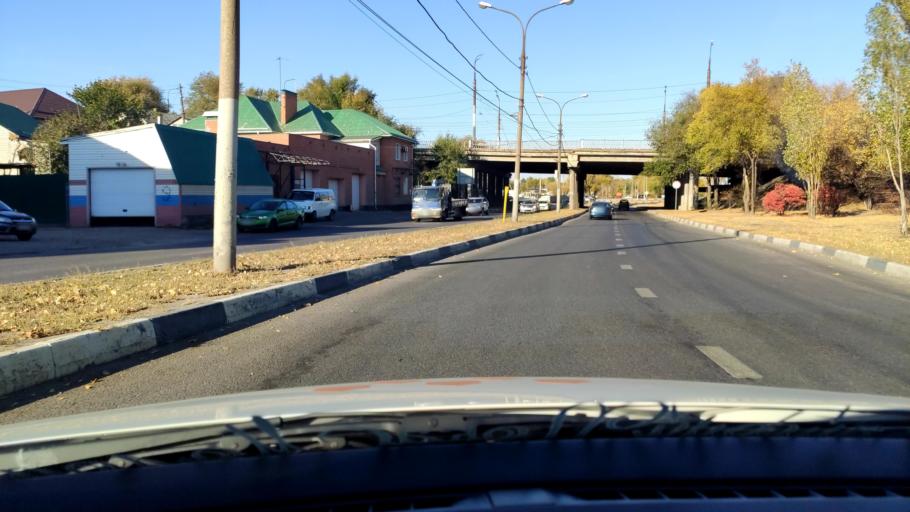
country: RU
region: Voronezj
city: Voronezh
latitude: 51.6362
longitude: 39.2080
